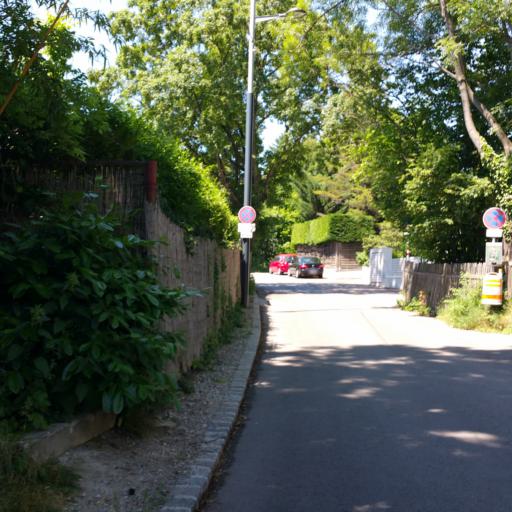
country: AT
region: Vienna
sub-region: Wien Stadt
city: Vienna
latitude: 48.2161
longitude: 16.2981
